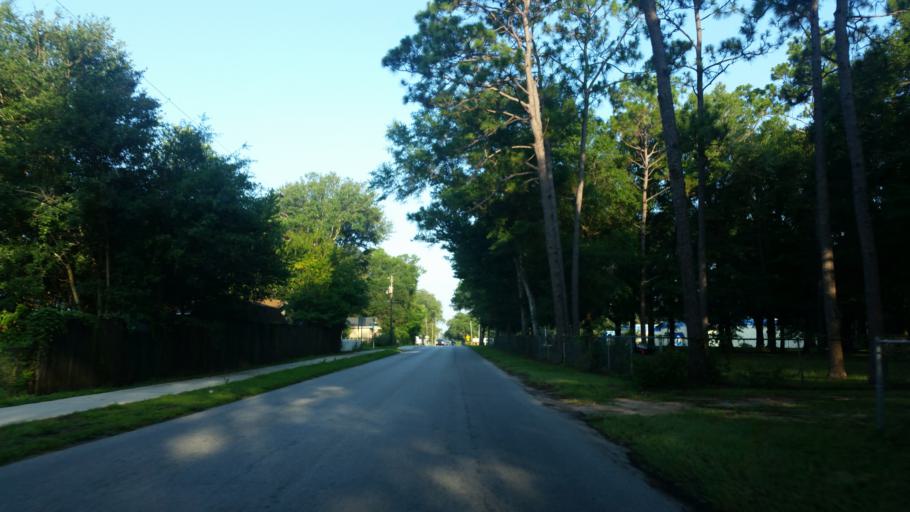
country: US
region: Florida
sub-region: Escambia County
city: Bellview
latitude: 30.4682
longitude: -87.2954
